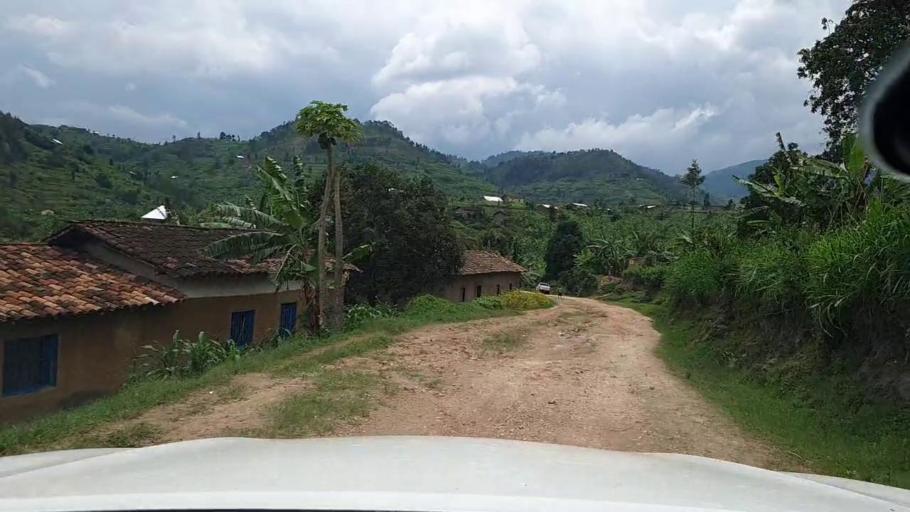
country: RW
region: Western Province
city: Kibuye
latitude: -2.0814
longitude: 29.4193
